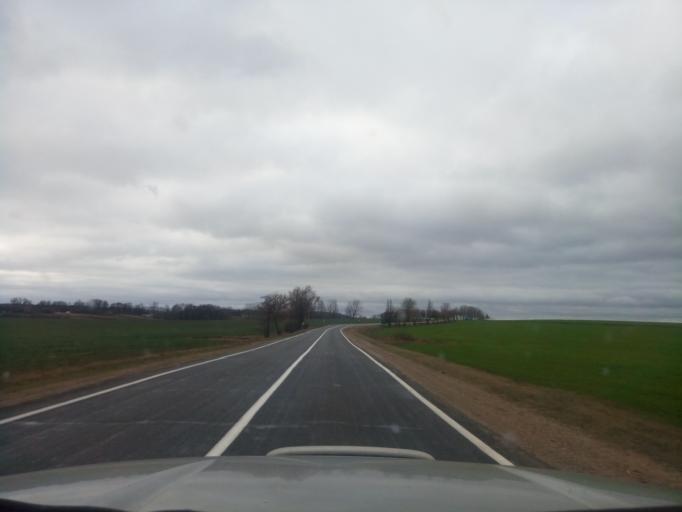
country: BY
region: Minsk
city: Kapyl'
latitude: 53.1862
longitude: 27.1813
